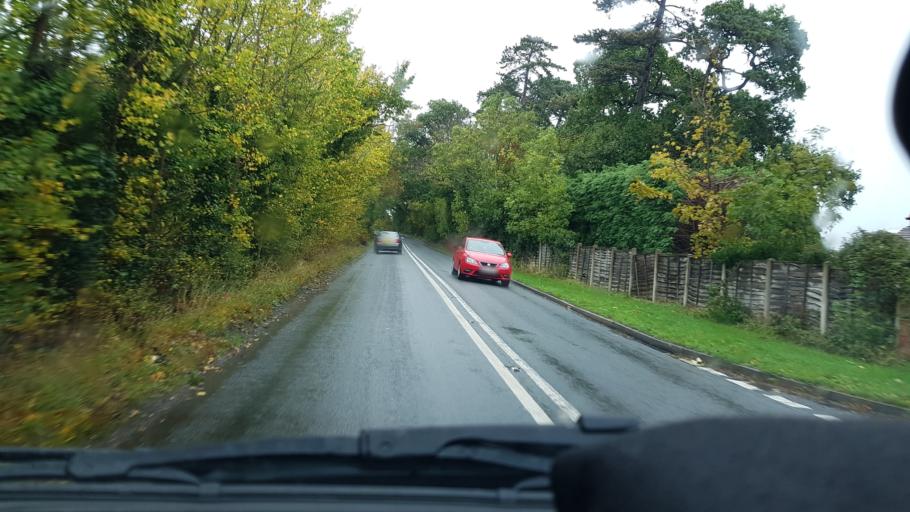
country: GB
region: England
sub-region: Worcestershire
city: Great Malvern
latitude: 52.0903
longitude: -2.3112
